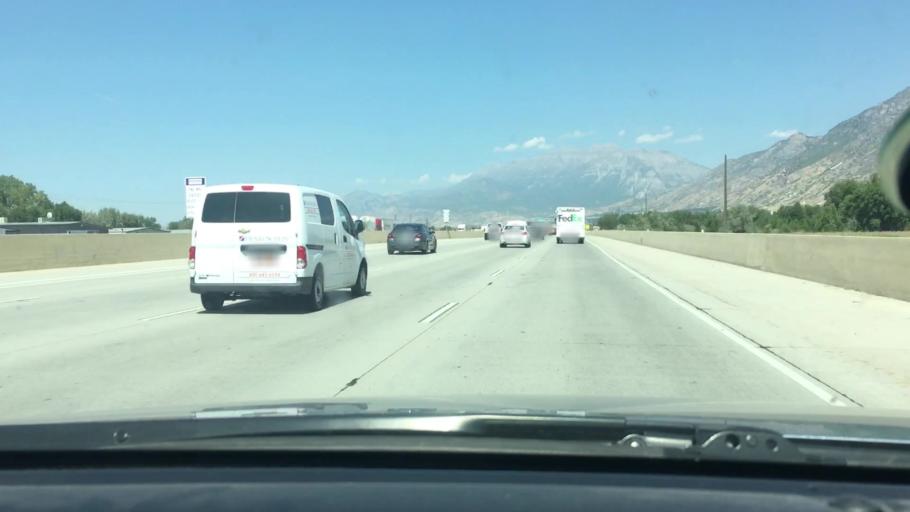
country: US
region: Utah
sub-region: Utah County
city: Springville
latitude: 40.1791
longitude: -111.6463
